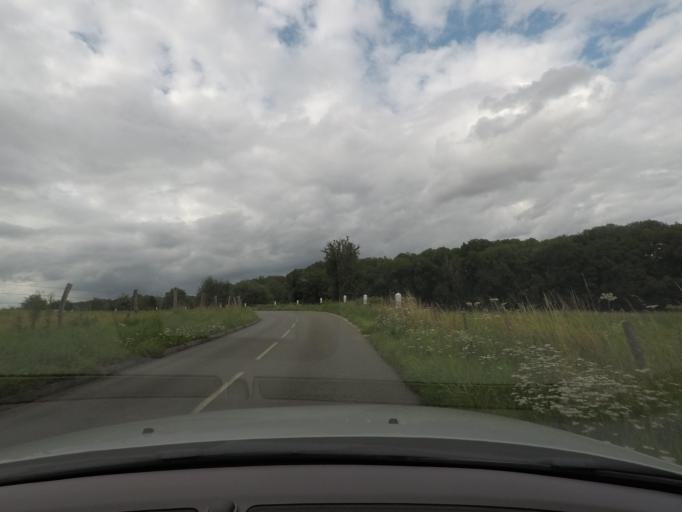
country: FR
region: Haute-Normandie
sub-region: Departement de l'Eure
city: Les Andelys
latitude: 49.2842
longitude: 1.3481
